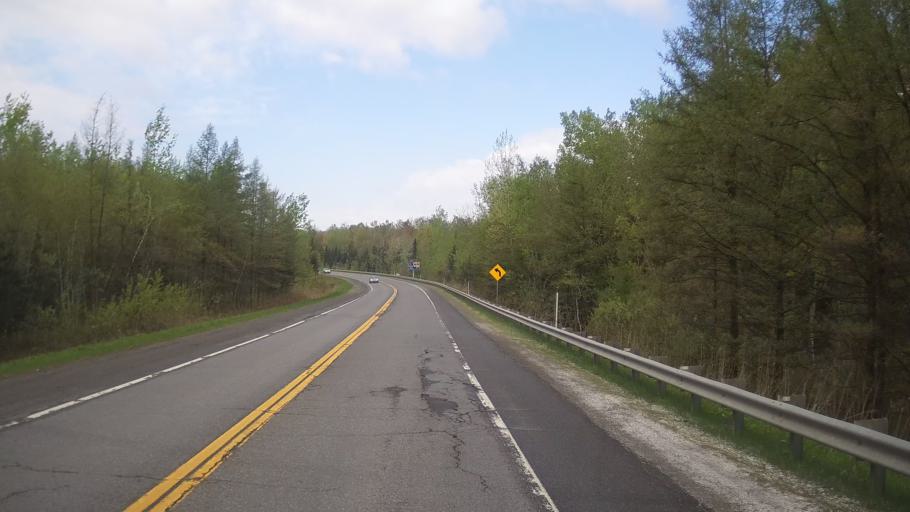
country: CA
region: Quebec
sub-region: Monteregie
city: Cowansville
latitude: 45.1982
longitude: -72.7250
